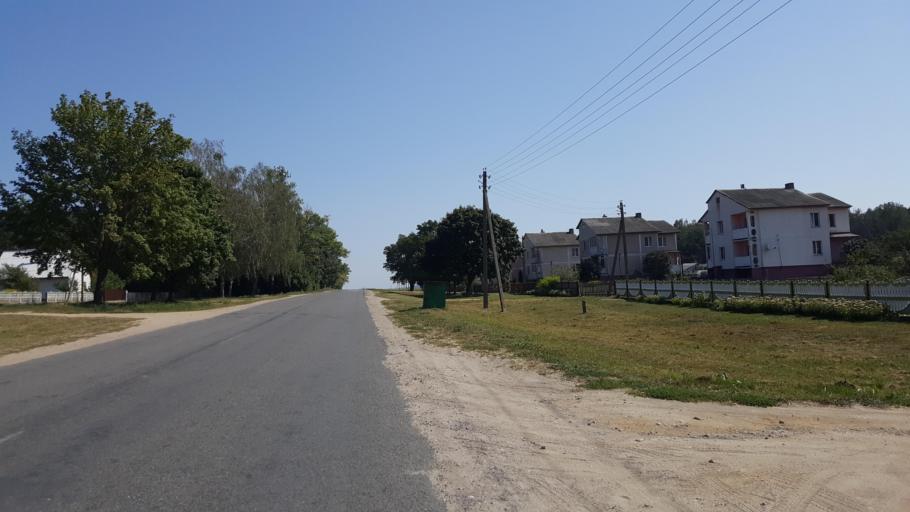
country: BY
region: Brest
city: Vysokaye
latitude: 52.4410
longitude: 23.4663
